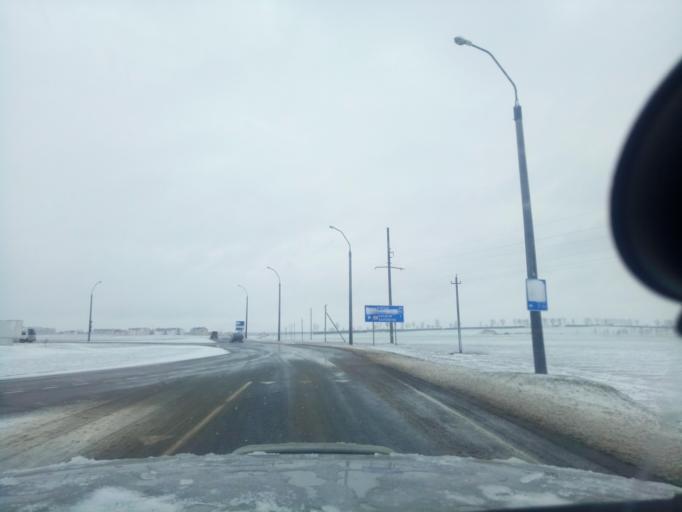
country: BY
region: Minsk
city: Nyasvizh
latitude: 53.2386
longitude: 26.6333
